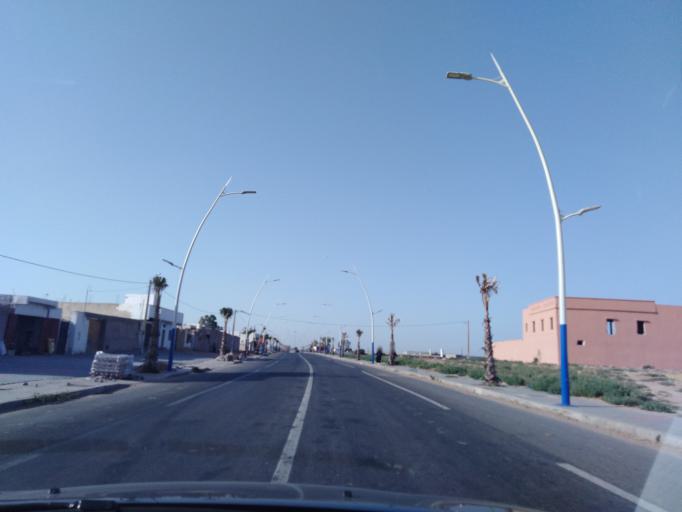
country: MA
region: Doukkala-Abda
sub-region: El-Jadida
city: Sidi Bennour
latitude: 32.5850
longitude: -8.7114
